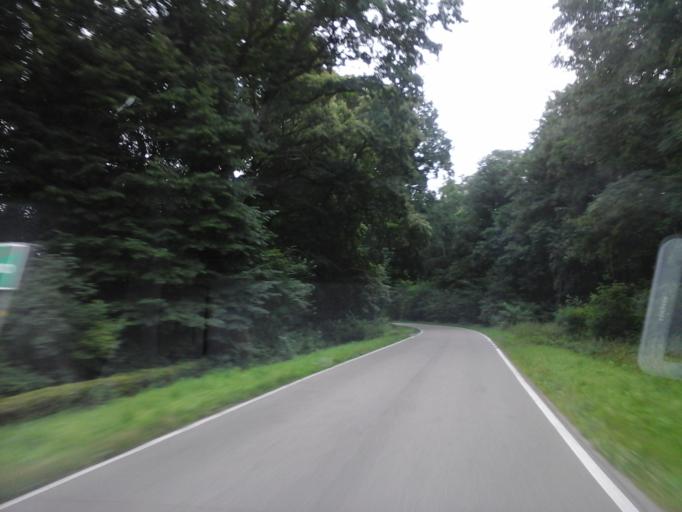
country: PL
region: West Pomeranian Voivodeship
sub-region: Powiat choszczenski
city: Pelczyce
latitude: 53.0872
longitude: 15.2755
